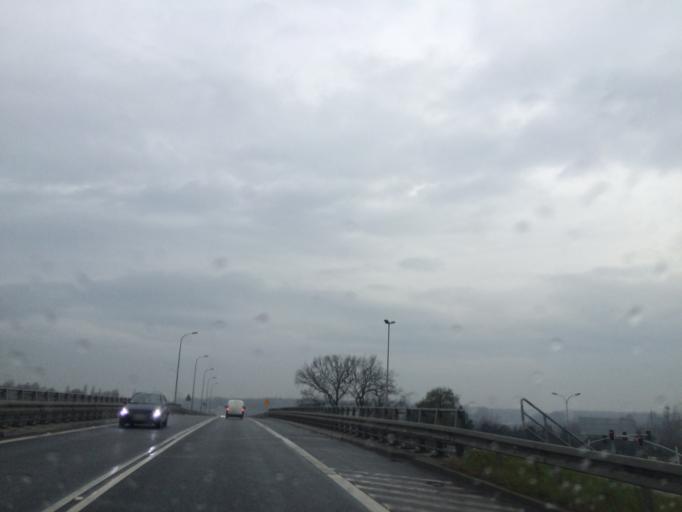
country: PL
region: Silesian Voivodeship
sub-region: Piekary Slaskie
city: Piekary Slaskie
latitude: 50.3685
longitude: 18.8976
